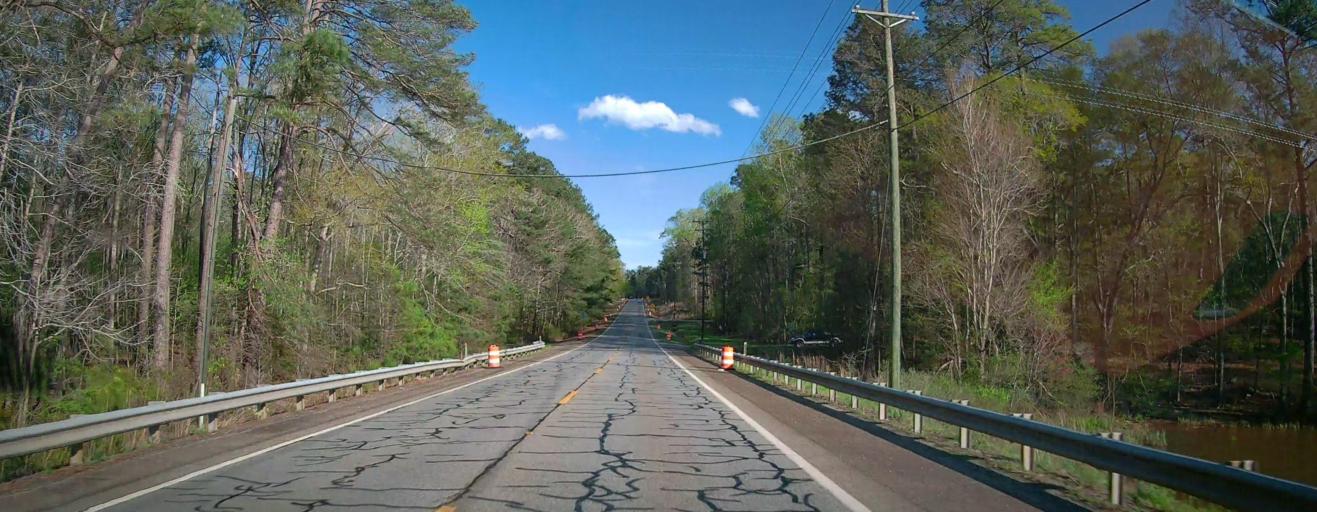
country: US
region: Georgia
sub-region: Putnam County
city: Eatonton
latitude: 33.1630
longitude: -83.3742
